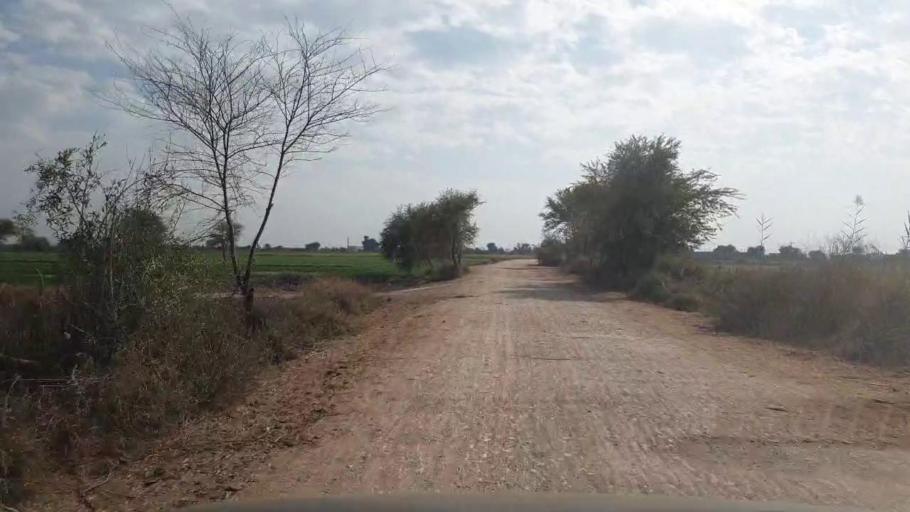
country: PK
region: Sindh
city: Sakrand
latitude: 26.0040
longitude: 68.4047
